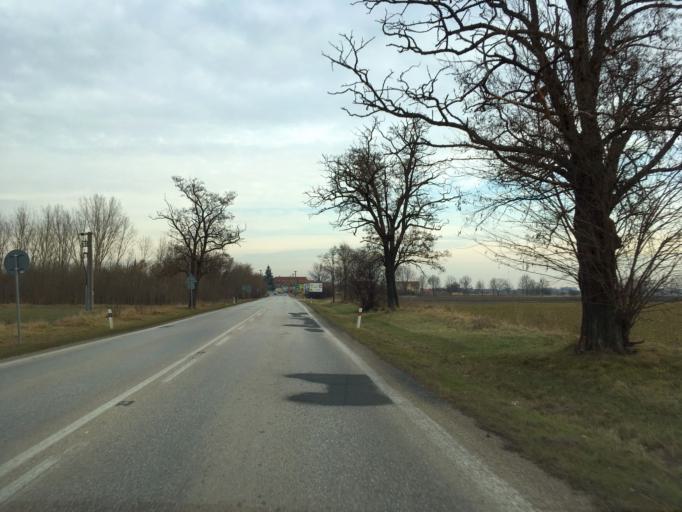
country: SK
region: Nitriansky
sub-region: Okres Nove Zamky
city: Nove Zamky
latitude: 47.9971
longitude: 18.2557
